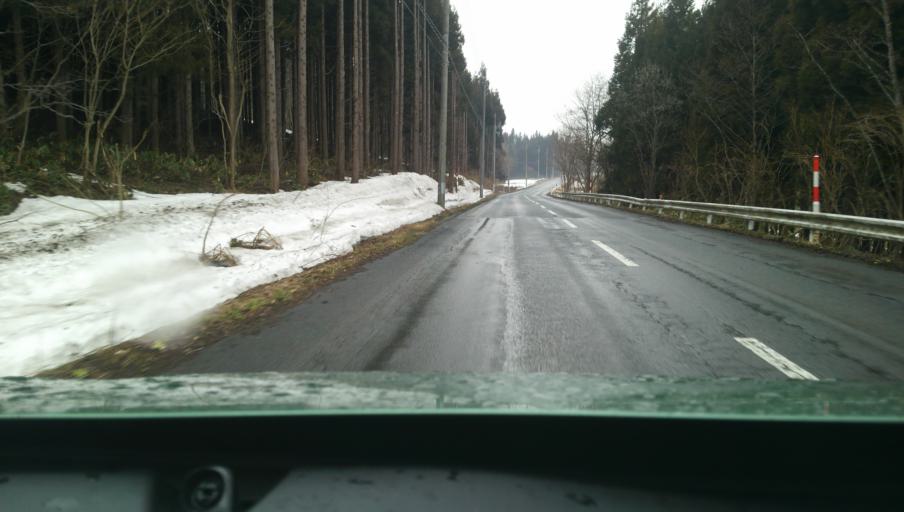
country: JP
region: Iwate
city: Kitakami
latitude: 39.2814
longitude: 140.9765
